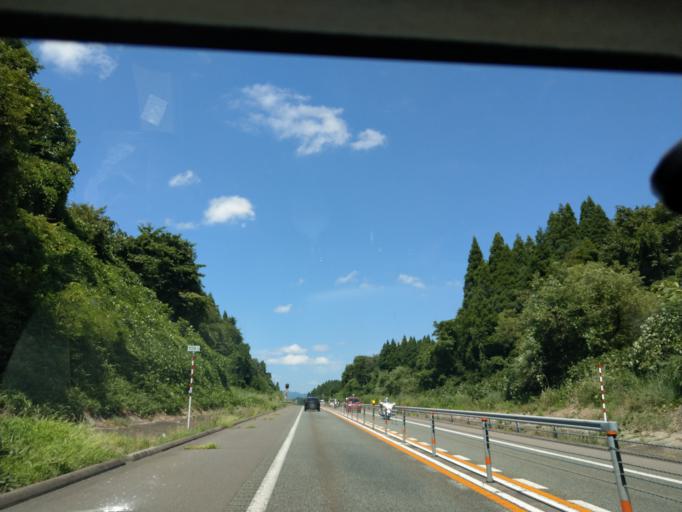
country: JP
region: Akita
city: Akita
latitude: 39.6827
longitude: 140.1856
